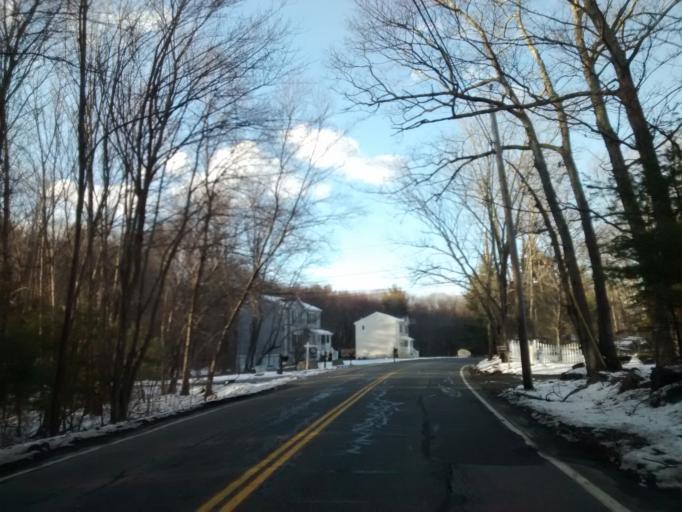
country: US
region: Massachusetts
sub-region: Middlesex County
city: Hopkinton
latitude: 42.1901
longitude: -71.5050
